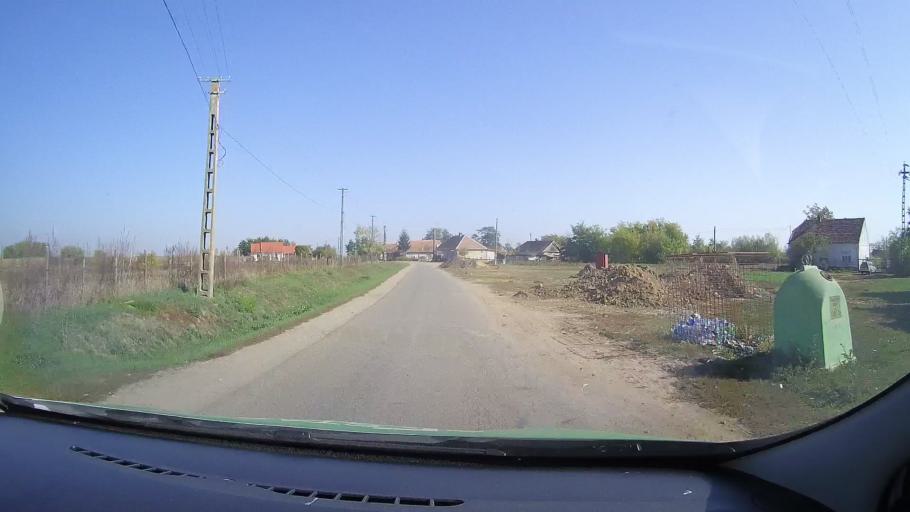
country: RO
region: Satu Mare
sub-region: Comuna Ciumesti
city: Ciumesti
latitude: 47.6702
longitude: 22.3401
